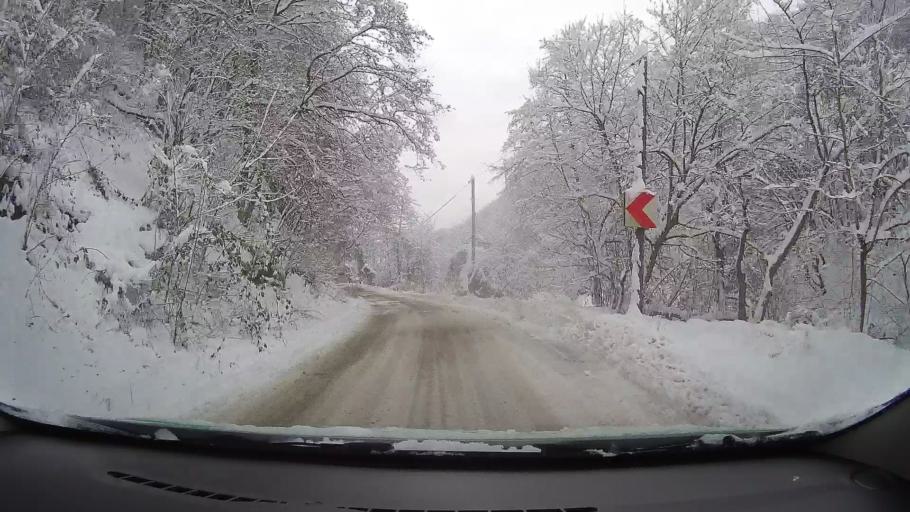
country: RO
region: Alba
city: Pianu de Sus
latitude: 45.8694
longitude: 23.4953
